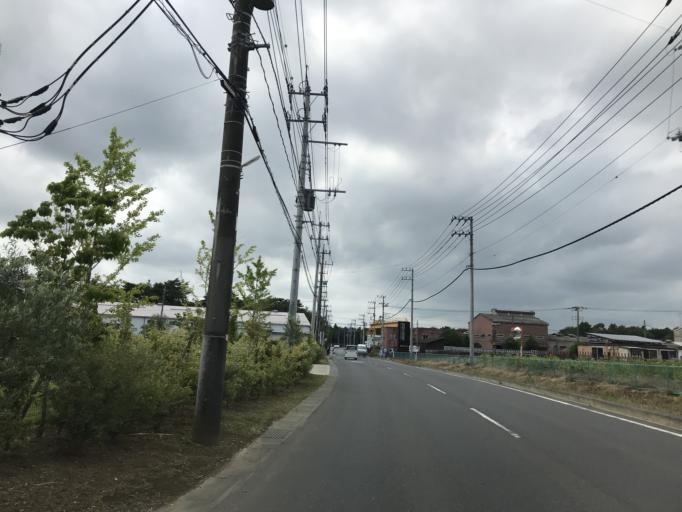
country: JP
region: Ibaraki
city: Ushiku
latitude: 35.9784
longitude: 140.0730
